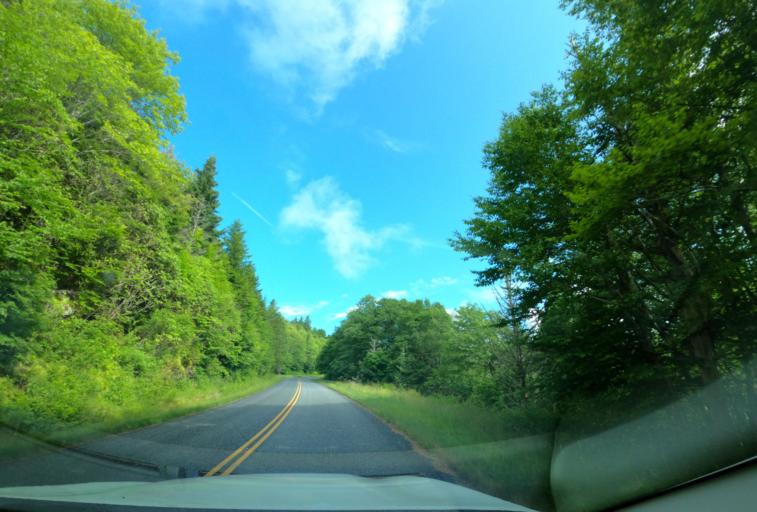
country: US
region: North Carolina
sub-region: Haywood County
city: Hazelwood
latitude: 35.3196
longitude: -82.9636
